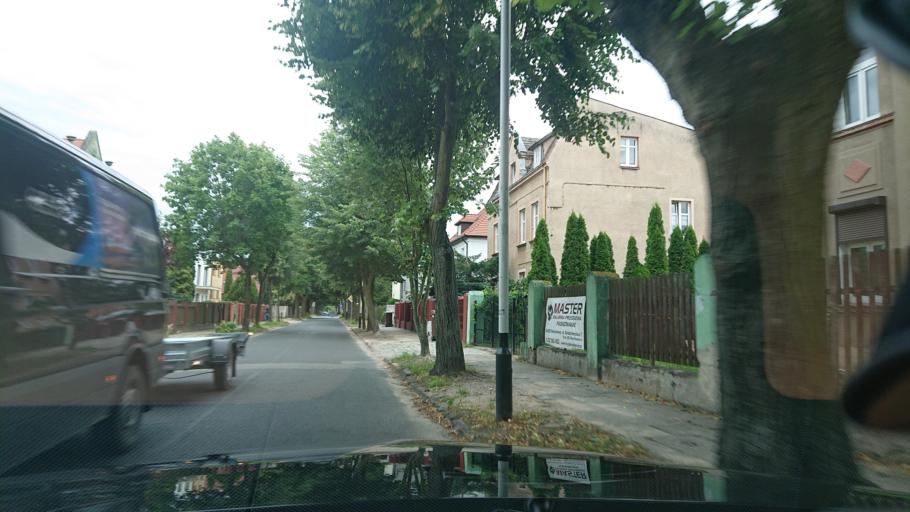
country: PL
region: Greater Poland Voivodeship
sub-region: Powiat gnieznienski
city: Gniezno
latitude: 52.5353
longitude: 17.6160
